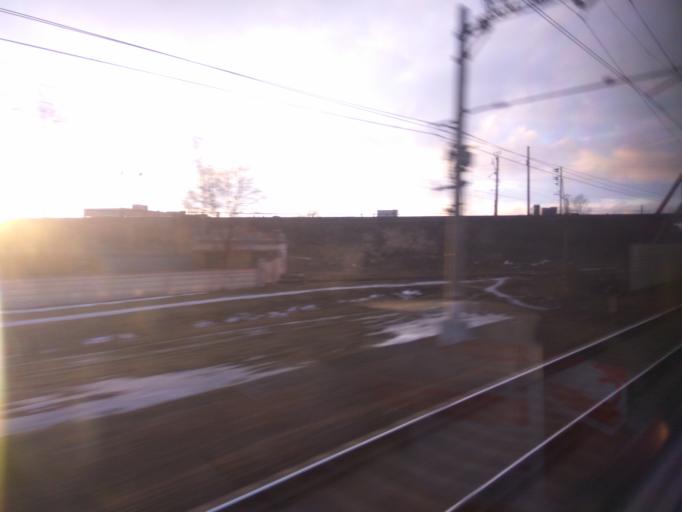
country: RU
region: St.-Petersburg
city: Centralniy
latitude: 59.9015
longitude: 30.3806
